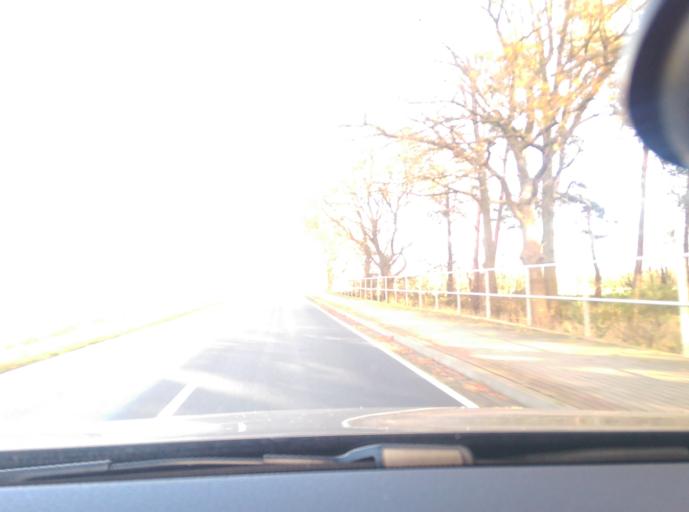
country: DE
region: Lower Saxony
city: Wietze
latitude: 52.6682
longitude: 9.7731
